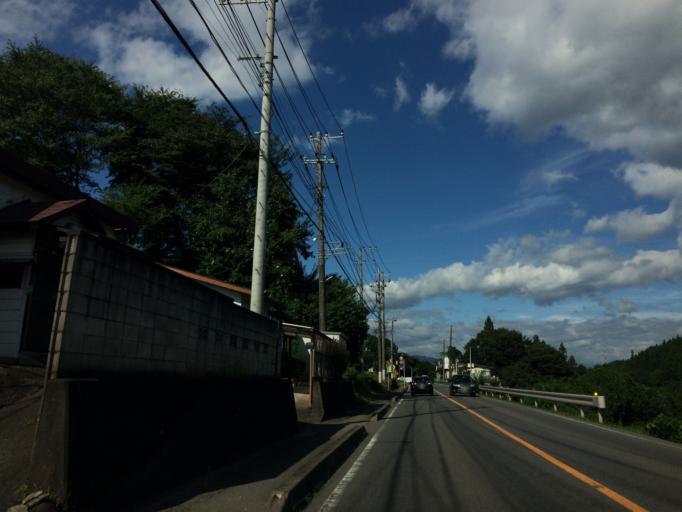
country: JP
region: Gunma
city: Nakanojomachi
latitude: 36.5506
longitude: 138.8074
